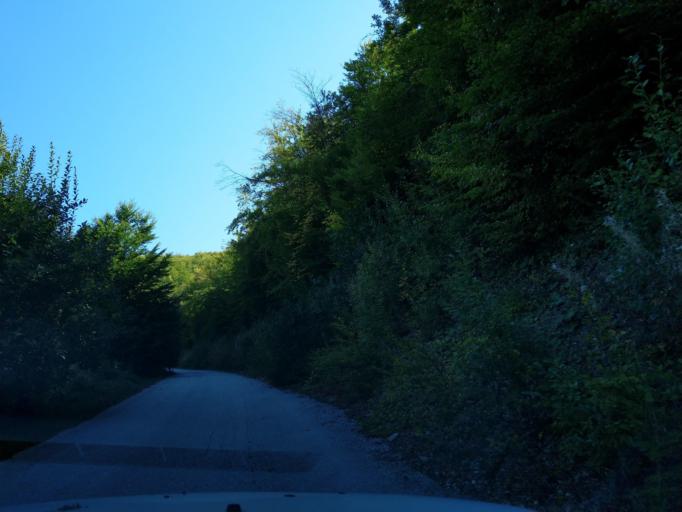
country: RS
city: Sokolovica
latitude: 43.2568
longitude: 20.3023
